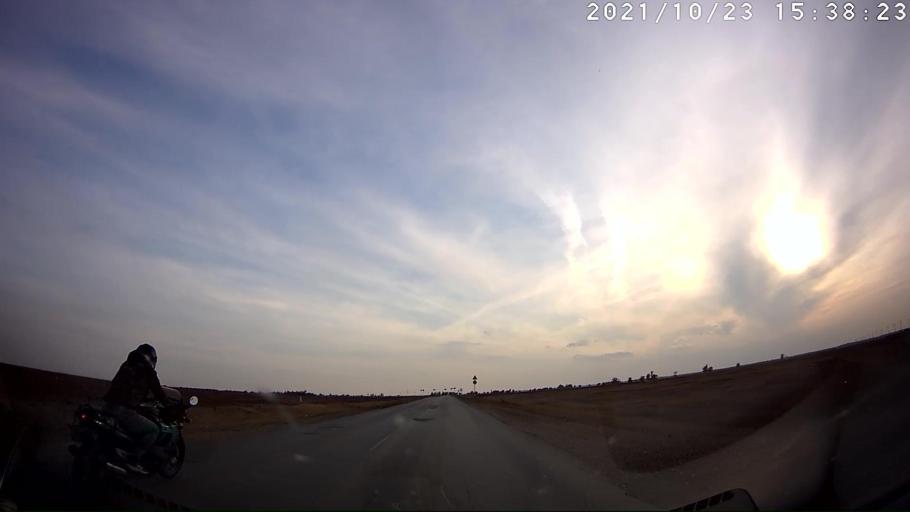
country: RU
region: Volgograd
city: Bereslavka
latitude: 48.1349
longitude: 44.1204
